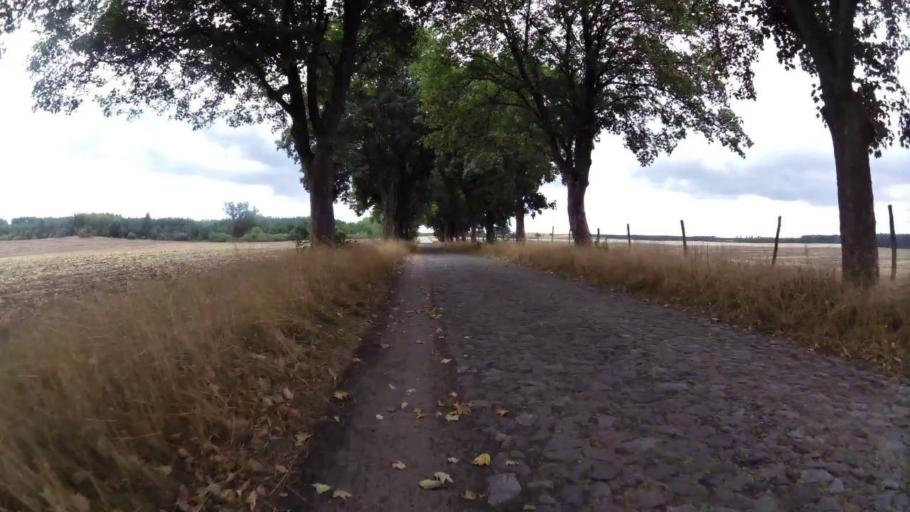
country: PL
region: West Pomeranian Voivodeship
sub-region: Powiat mysliborski
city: Debno
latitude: 52.8388
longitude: 14.7138
